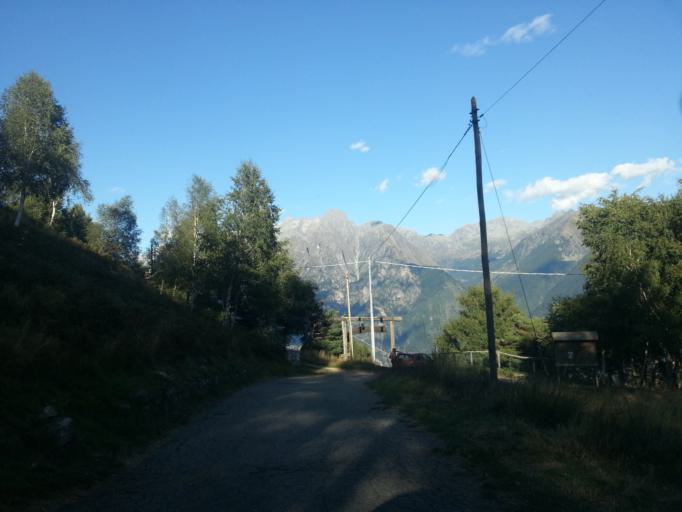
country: IT
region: Lombardy
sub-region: Provincia di Como
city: Sorico
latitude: 46.1932
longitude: 9.3952
